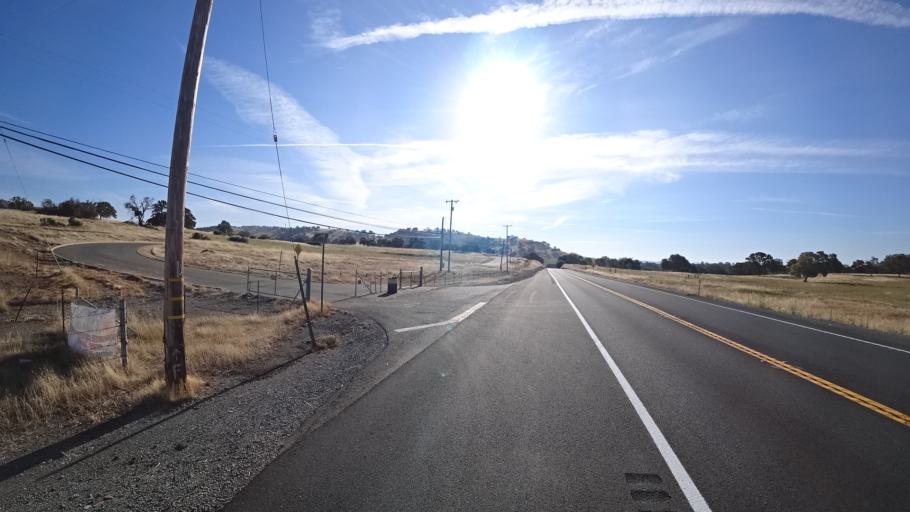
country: US
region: California
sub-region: Calaveras County
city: San Andreas
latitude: 38.2123
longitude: -120.7551
